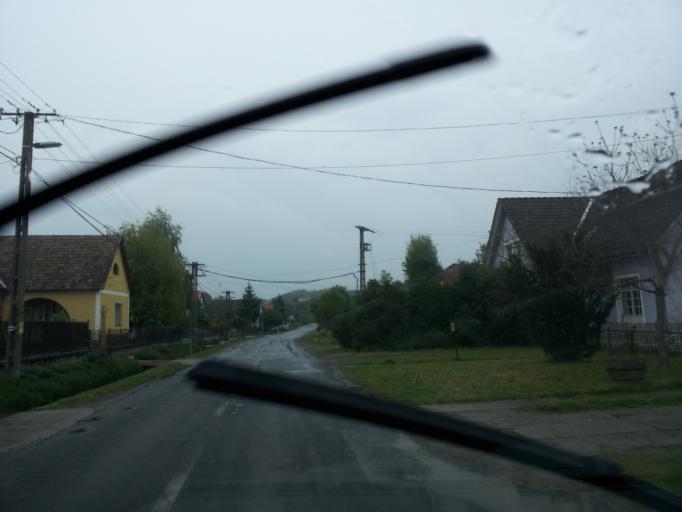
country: HU
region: Tolna
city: Szentgalpuszta
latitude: 46.2799
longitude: 18.6426
